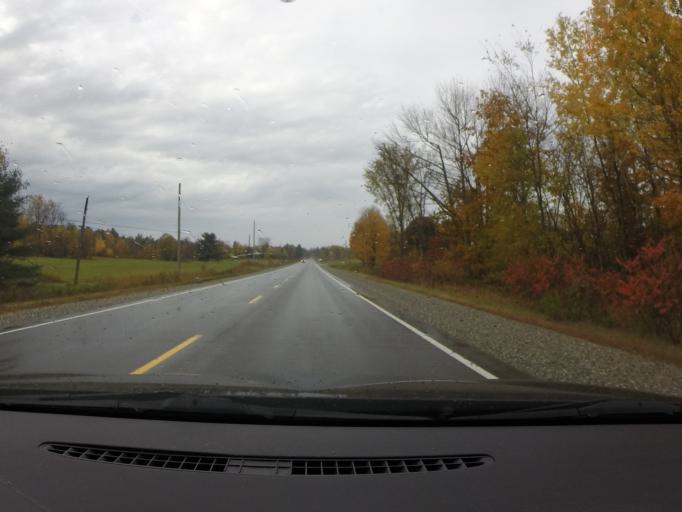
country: CA
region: Ontario
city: Perth
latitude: 44.8166
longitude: -76.6263
